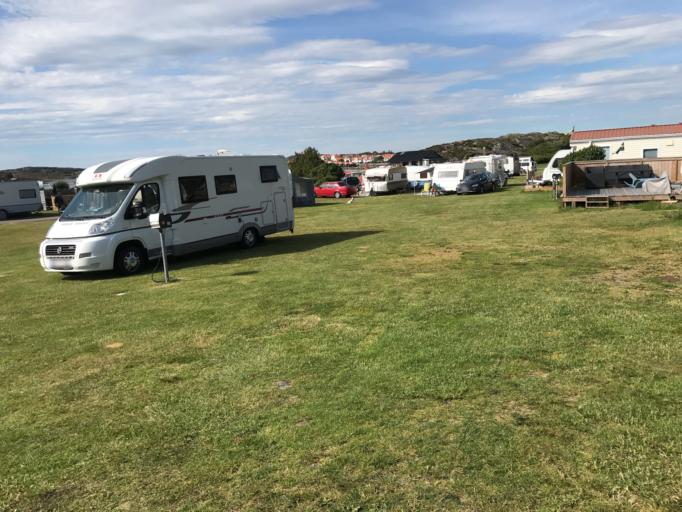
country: SE
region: Vaestra Goetaland
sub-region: Lysekils Kommun
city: Lysekil
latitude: 58.1444
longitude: 11.4168
